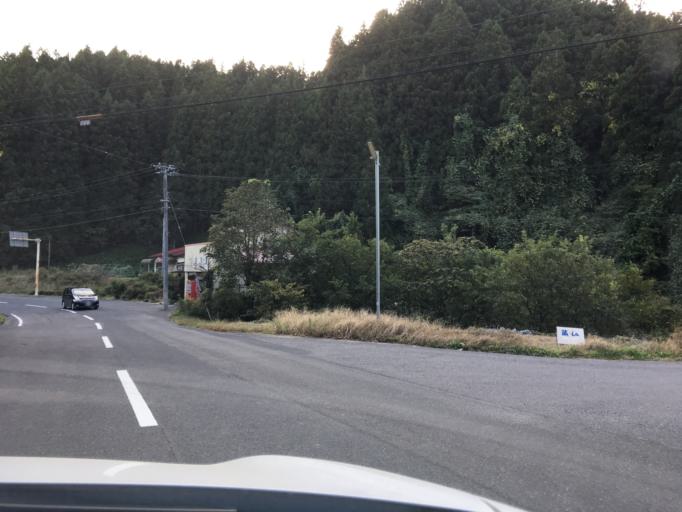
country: JP
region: Fukushima
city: Ishikawa
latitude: 37.2042
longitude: 140.5867
